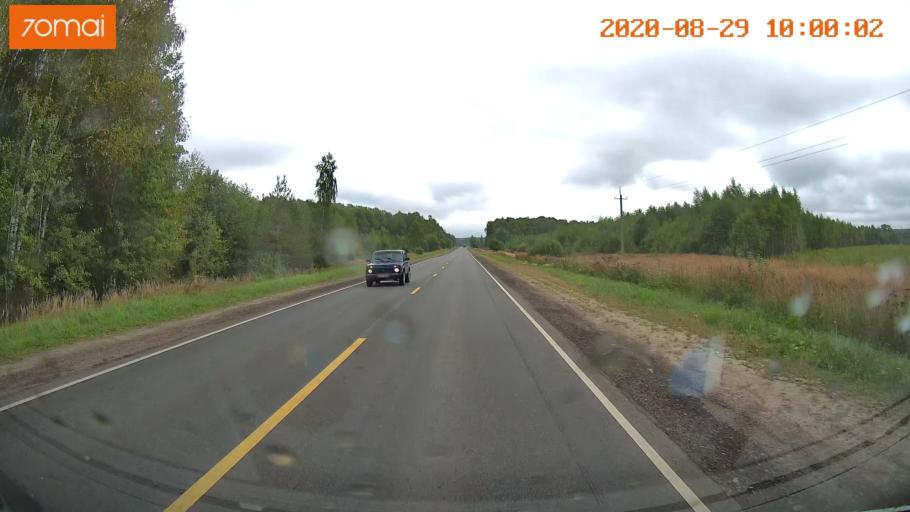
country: RU
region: Ivanovo
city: Zarechnyy
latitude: 57.4102
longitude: 42.3821
